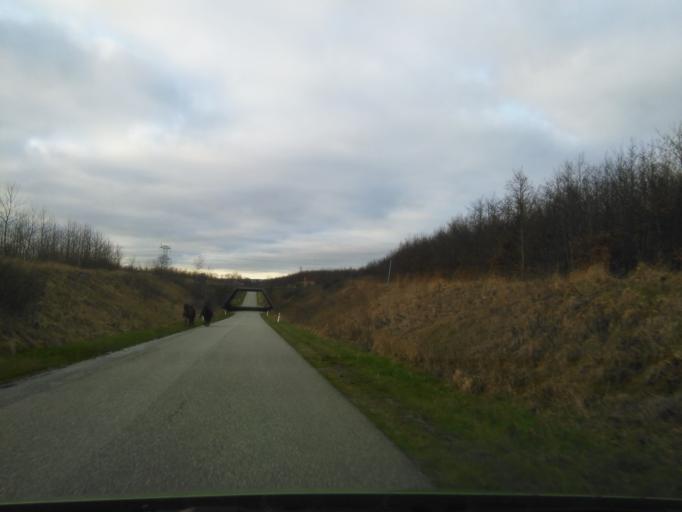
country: DK
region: Central Jutland
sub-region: Arhus Kommune
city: Sabro
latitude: 56.1819
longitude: 10.0716
